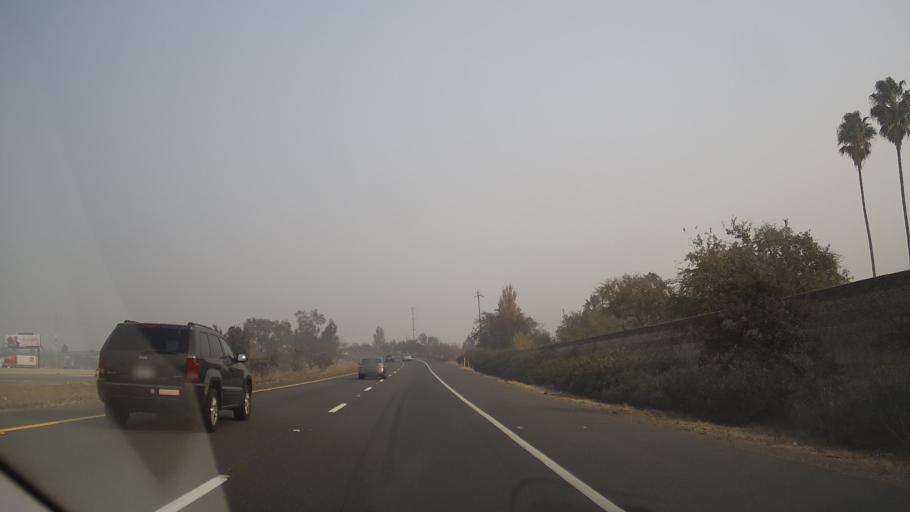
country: US
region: California
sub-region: Yolo County
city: West Sacramento
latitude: 38.5731
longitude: -121.5711
